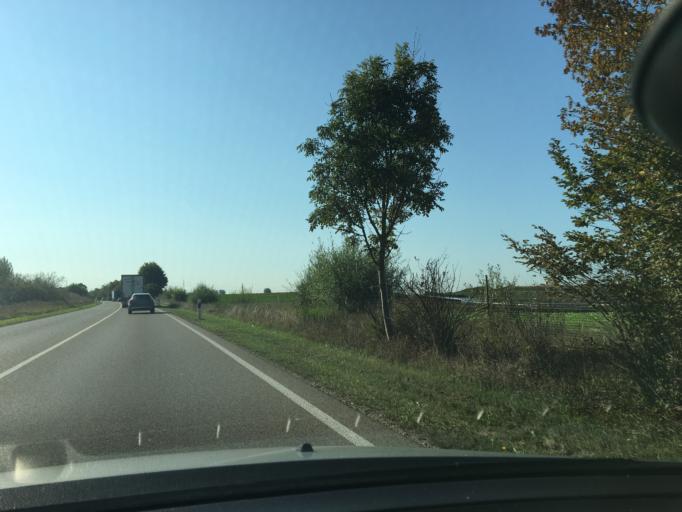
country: DE
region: Bavaria
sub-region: Upper Bavaria
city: Oberding
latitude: 48.3471
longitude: 11.8537
